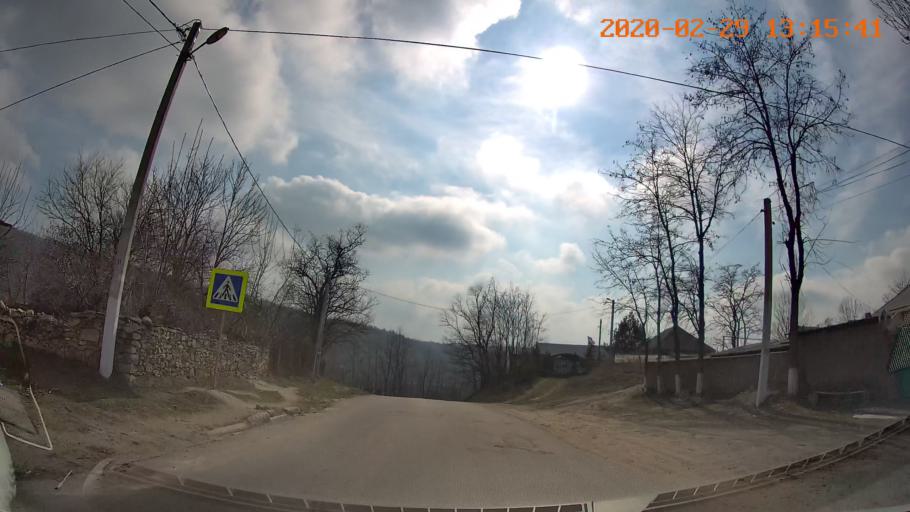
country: MD
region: Telenesti
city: Camenca
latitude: 48.0083
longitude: 28.6682
